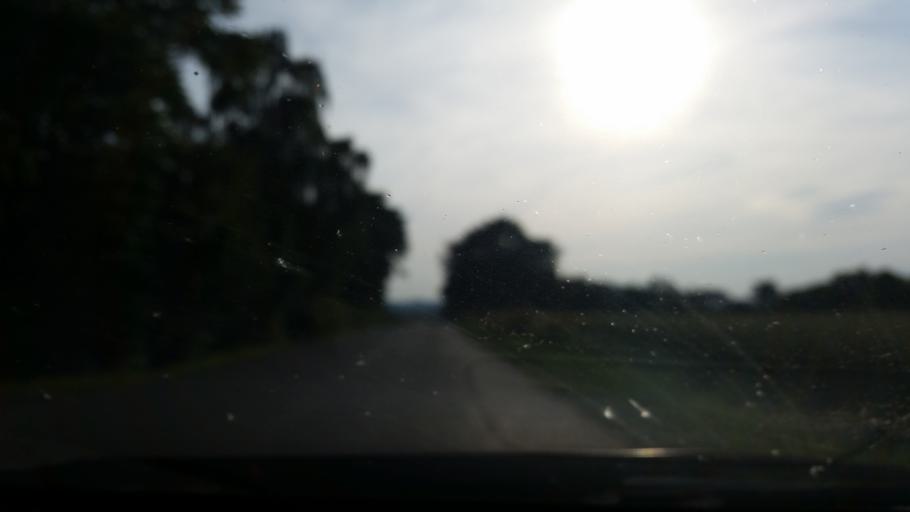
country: DK
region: Central Jutland
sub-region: Odder Kommune
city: Odder
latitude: 55.8907
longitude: 10.1574
